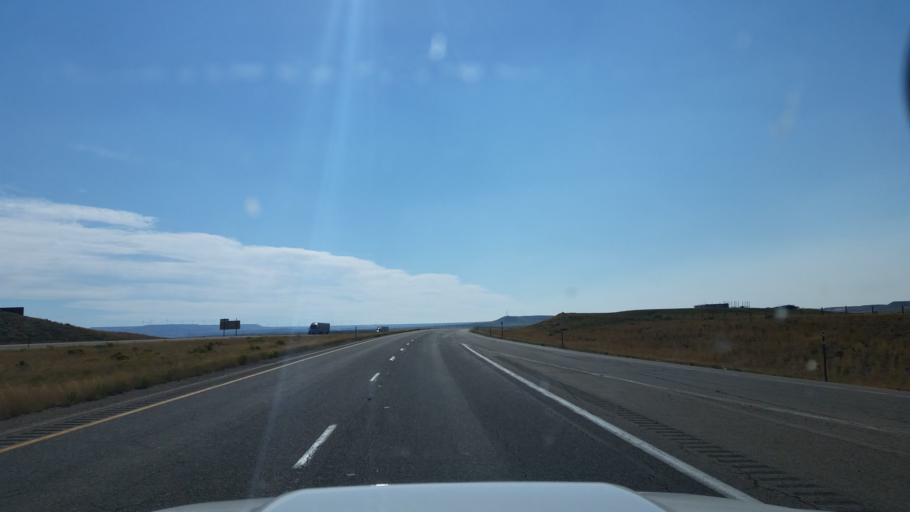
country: US
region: Wyoming
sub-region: Uinta County
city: Lyman
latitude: 41.3558
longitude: -110.3426
